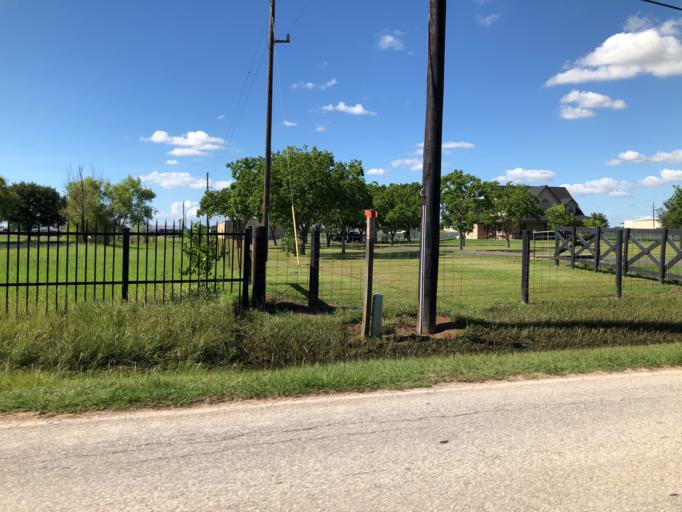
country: US
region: Texas
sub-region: Harris County
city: Katy
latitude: 29.8313
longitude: -95.8202
